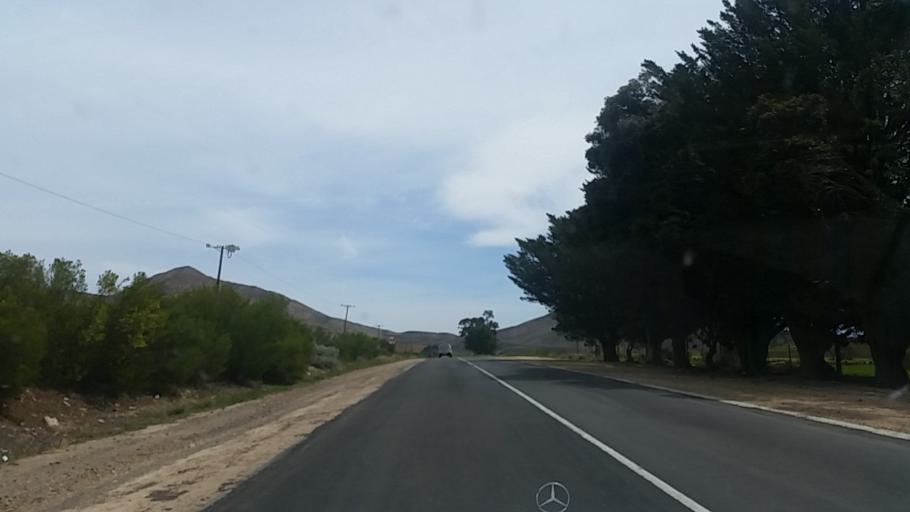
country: ZA
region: Western Cape
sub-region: Eden District Municipality
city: George
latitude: -33.8193
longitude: 22.3619
